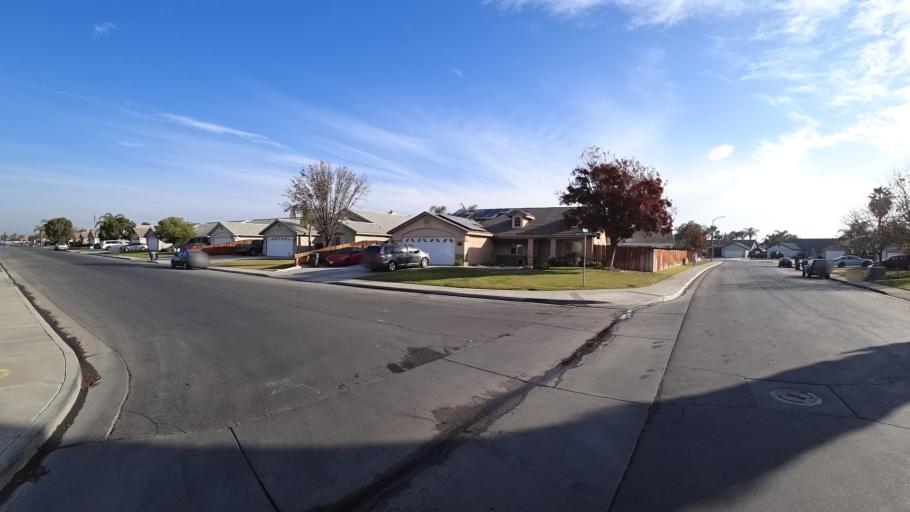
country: US
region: California
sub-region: Kern County
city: Rosedale
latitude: 35.4035
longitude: -119.1419
